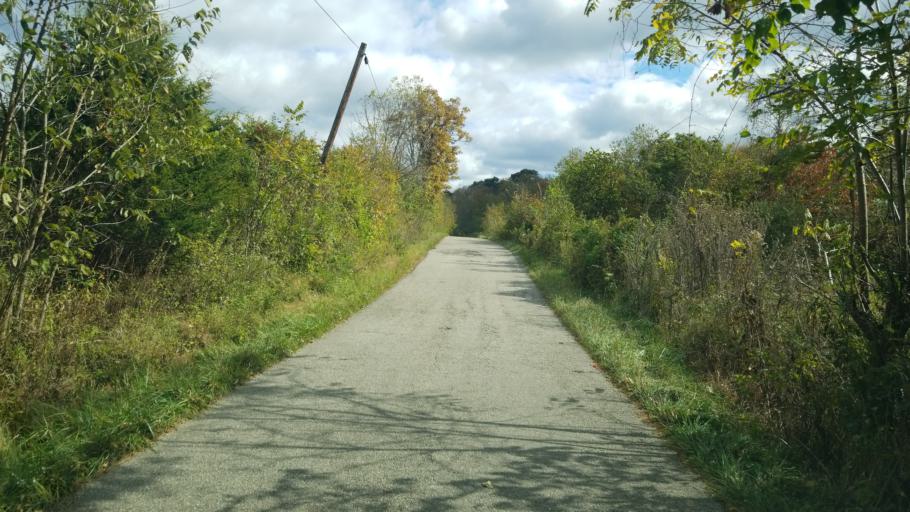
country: US
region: Ohio
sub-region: Jackson County
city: Jackson
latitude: 39.0912
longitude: -82.5884
